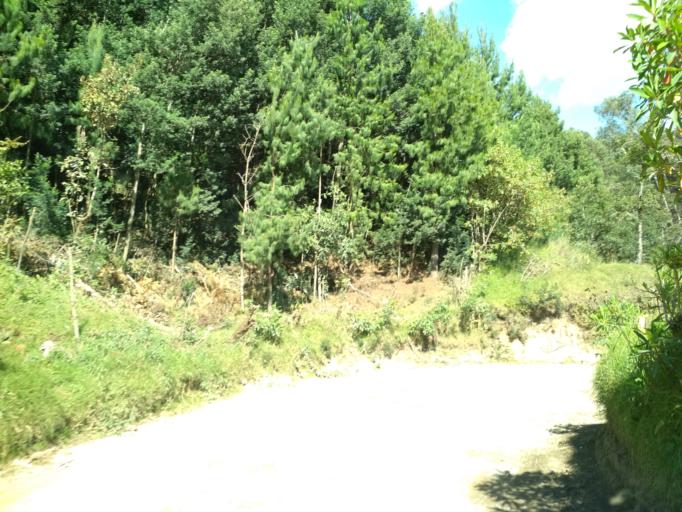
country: CO
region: Cauca
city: Jambalo
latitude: 2.7126
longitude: -76.3265
